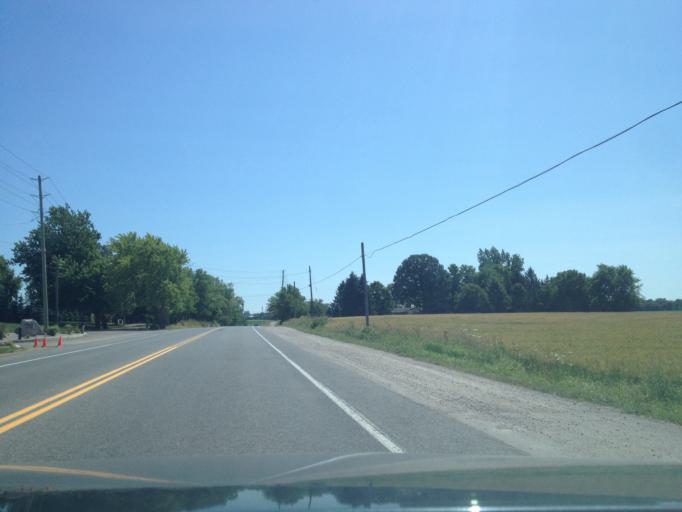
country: CA
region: Ontario
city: Waterloo
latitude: 43.5388
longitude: -80.5107
